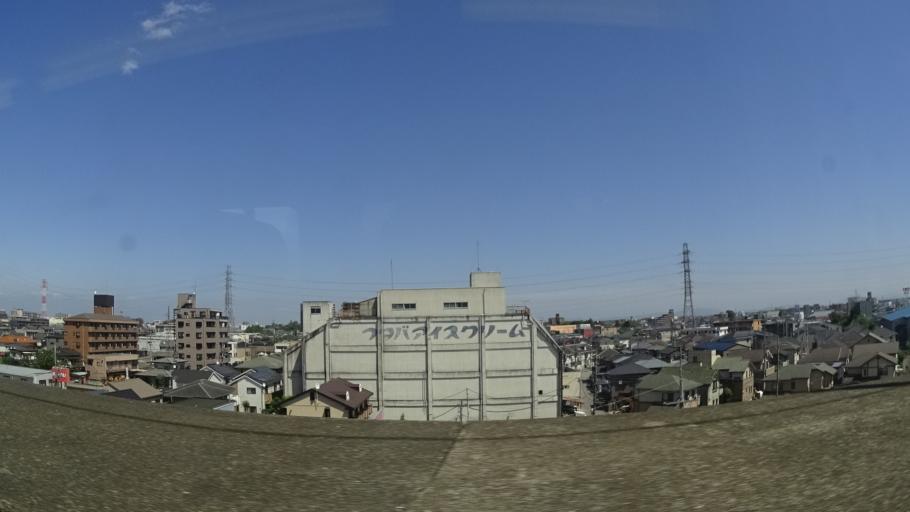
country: JP
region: Tochigi
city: Utsunomiya-shi
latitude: 36.5482
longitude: 139.8955
